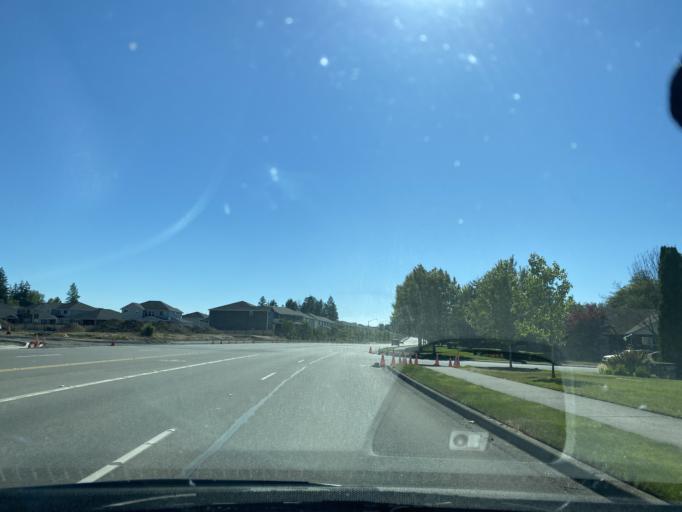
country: US
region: Washington
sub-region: Pierce County
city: McMillin
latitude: 47.1001
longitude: -122.2548
